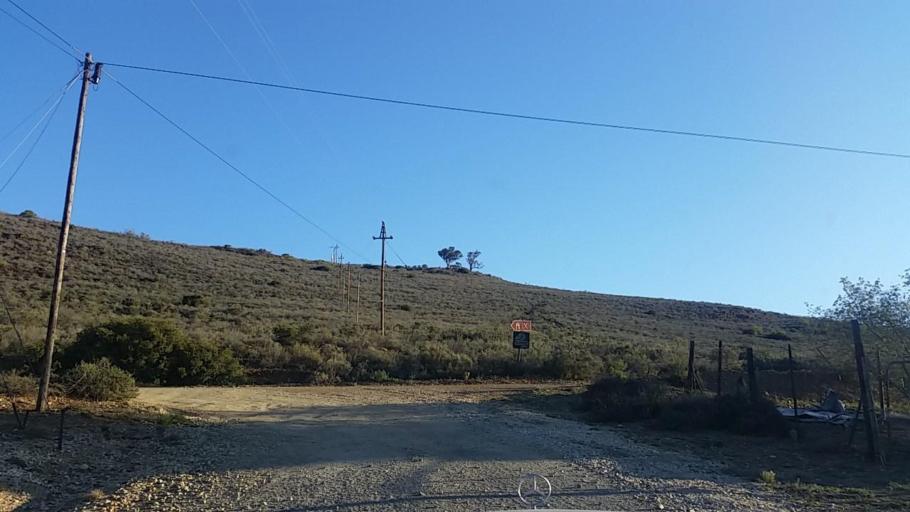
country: ZA
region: Western Cape
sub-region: Eden District Municipality
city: Knysna
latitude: -33.6565
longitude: 23.1342
